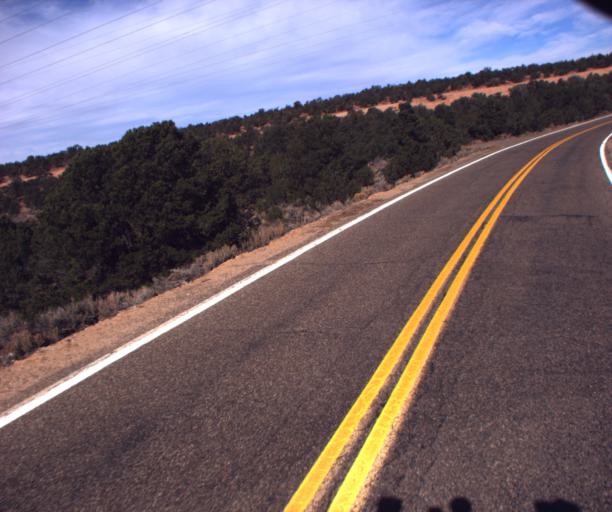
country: US
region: Arizona
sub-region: Navajo County
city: Kayenta
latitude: 36.6073
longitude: -110.5017
